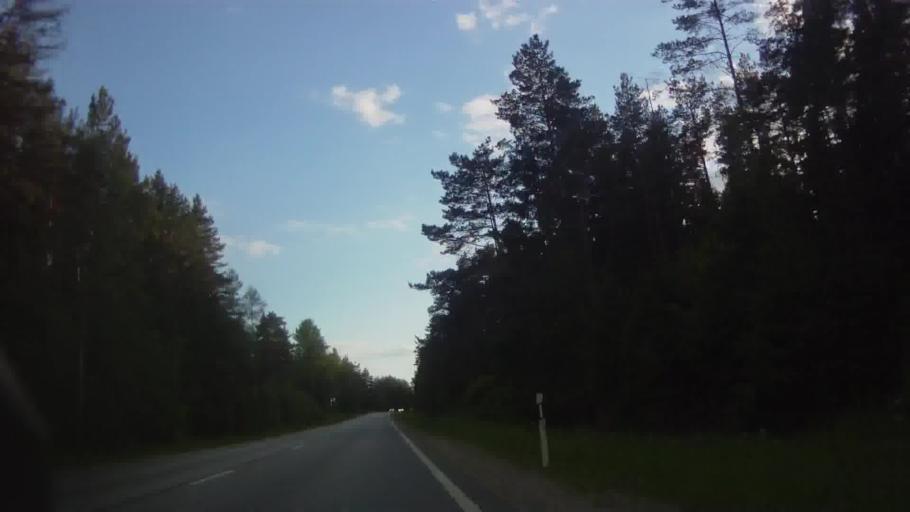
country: LV
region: Varaklani
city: Varaklani
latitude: 56.5720
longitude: 26.6533
